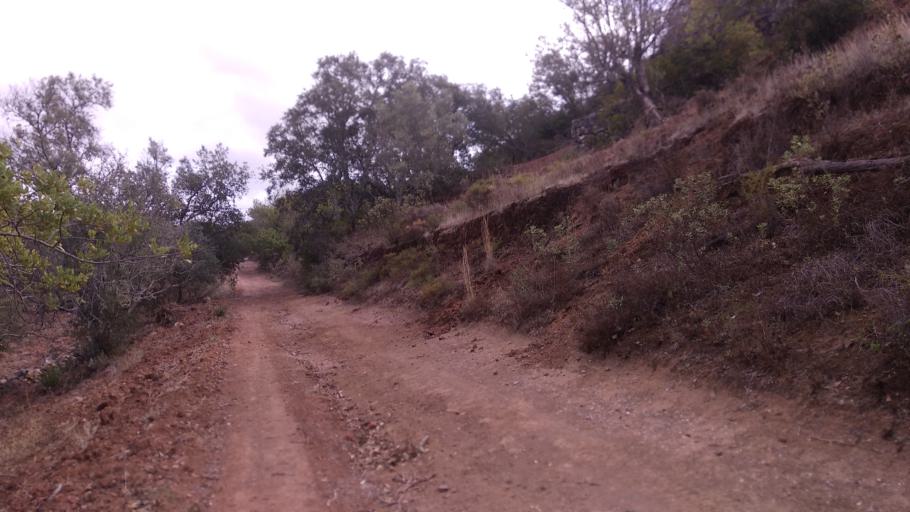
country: PT
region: Faro
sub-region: Sao Bras de Alportel
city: Sao Bras de Alportel
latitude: 37.1600
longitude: -7.9066
